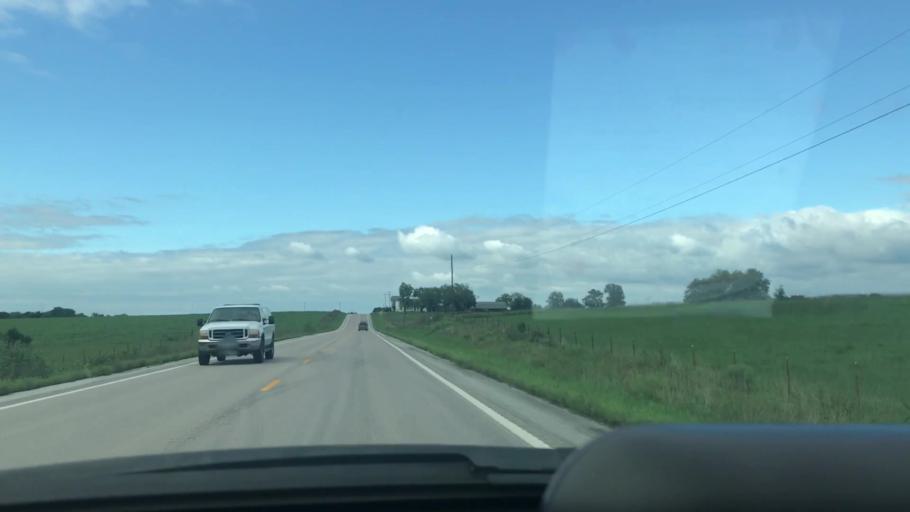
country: US
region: Missouri
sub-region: Hickory County
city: Hermitage
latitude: 37.9507
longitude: -93.2075
